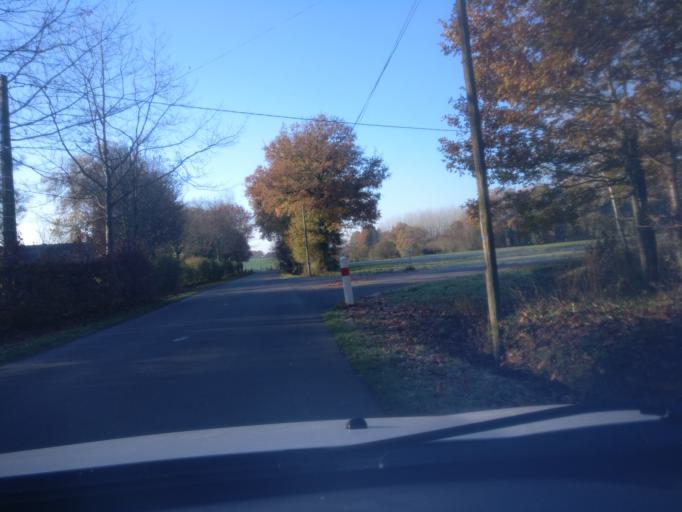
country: FR
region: Brittany
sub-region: Departement d'Ille-et-Vilaine
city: Chavagne
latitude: 48.0166
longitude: -1.7870
